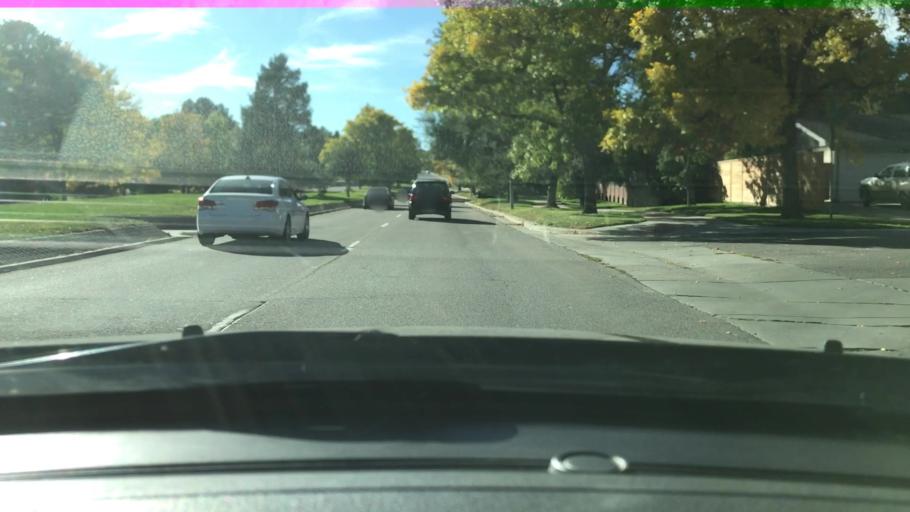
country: US
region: Colorado
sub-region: Arapahoe County
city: Glendale
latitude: 39.7114
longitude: -104.9164
